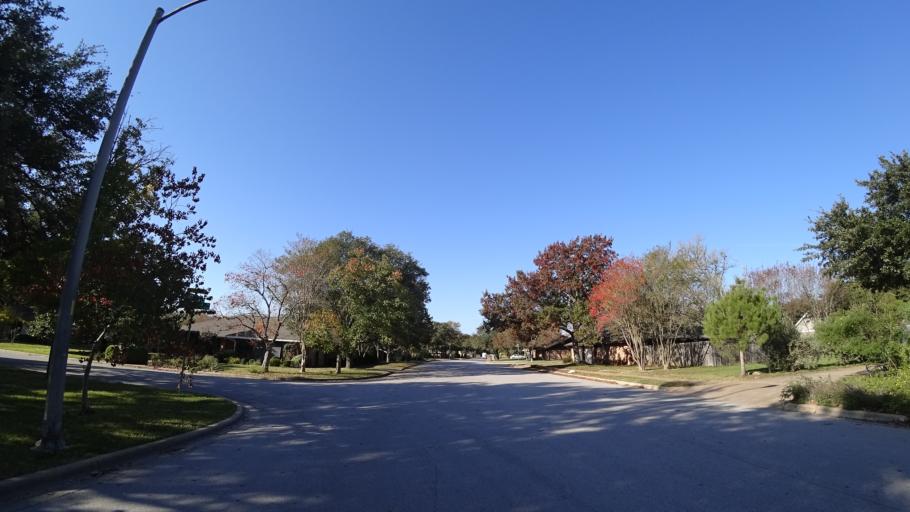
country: US
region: Texas
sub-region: Travis County
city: Shady Hollow
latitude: 30.2211
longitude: -97.8476
